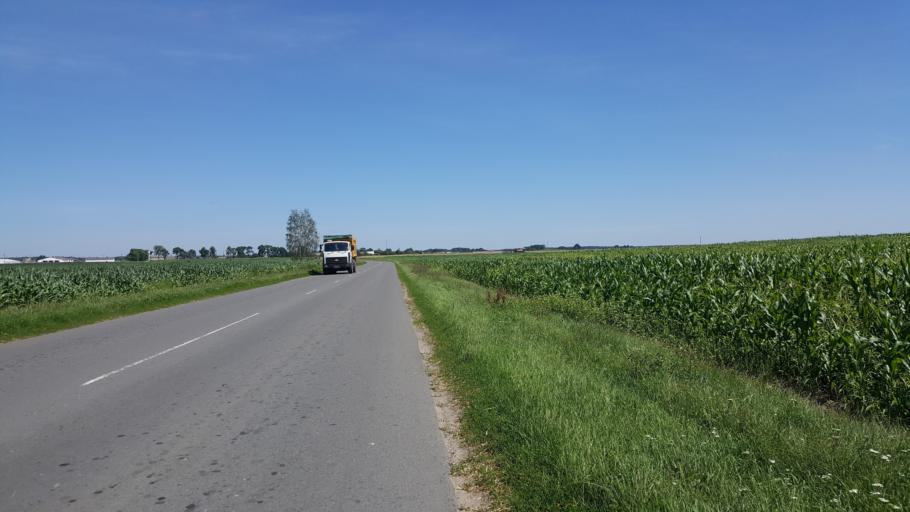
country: BY
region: Brest
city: Pruzhany
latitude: 52.5391
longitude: 24.2008
